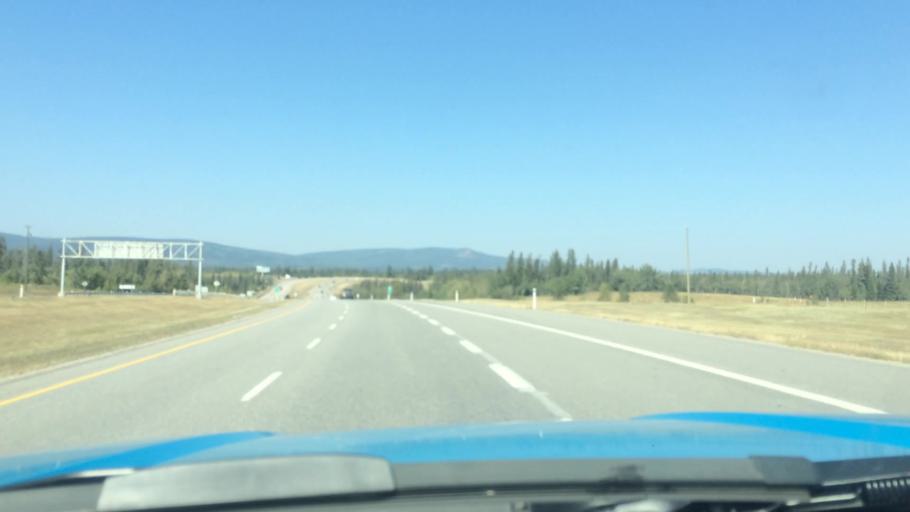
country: CA
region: Alberta
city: Canmore
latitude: 51.0805
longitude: -115.0556
